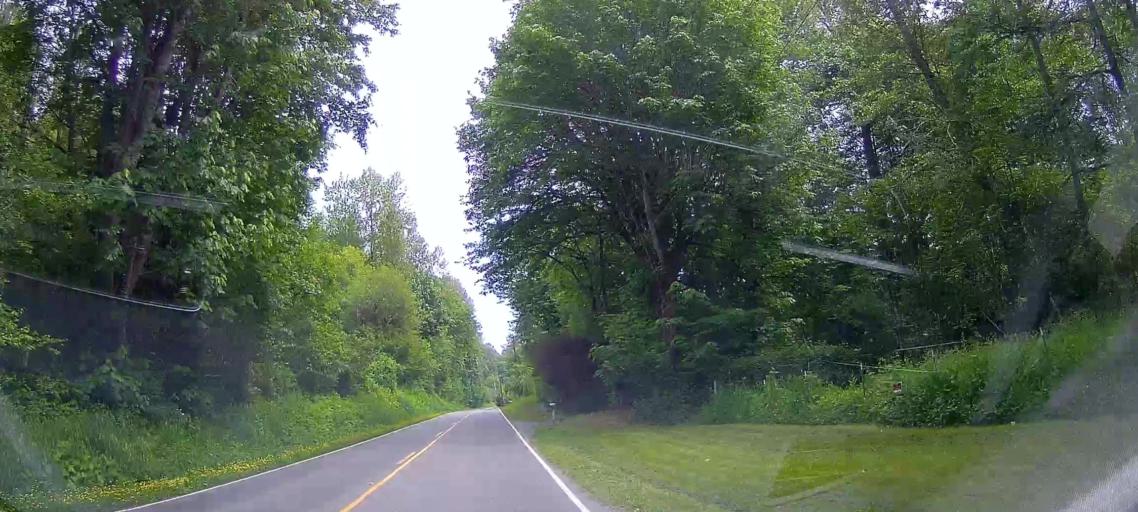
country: US
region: Washington
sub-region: Snohomish County
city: Bryant
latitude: 48.2369
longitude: -122.2111
